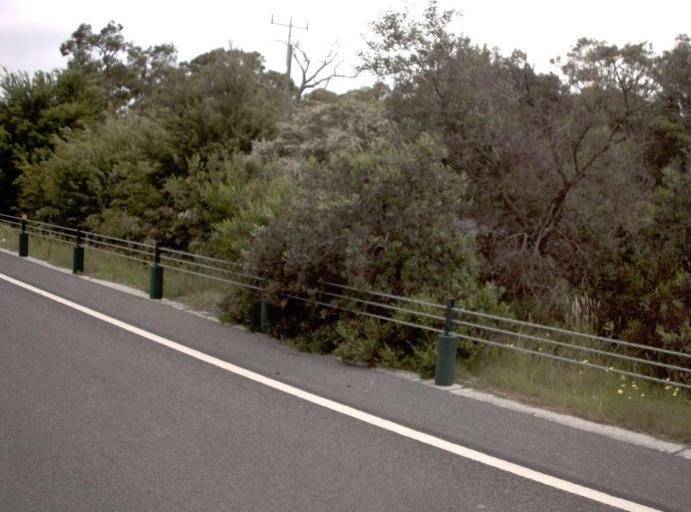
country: AU
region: Victoria
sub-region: Casey
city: Junction Village
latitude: -38.1271
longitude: 145.2905
